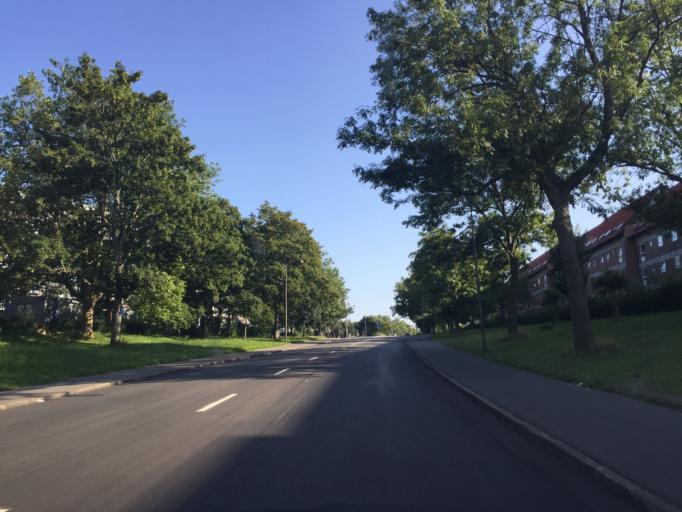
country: DK
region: Capital Region
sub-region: Kobenhavn
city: Copenhagen
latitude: 55.7096
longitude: 12.5554
